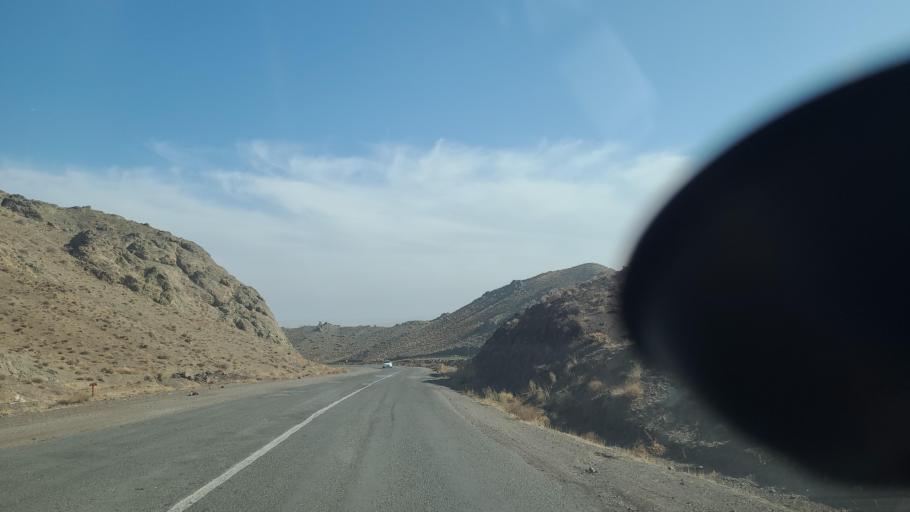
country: IR
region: Razavi Khorasan
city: Fariman
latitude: 35.5936
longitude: 59.7193
